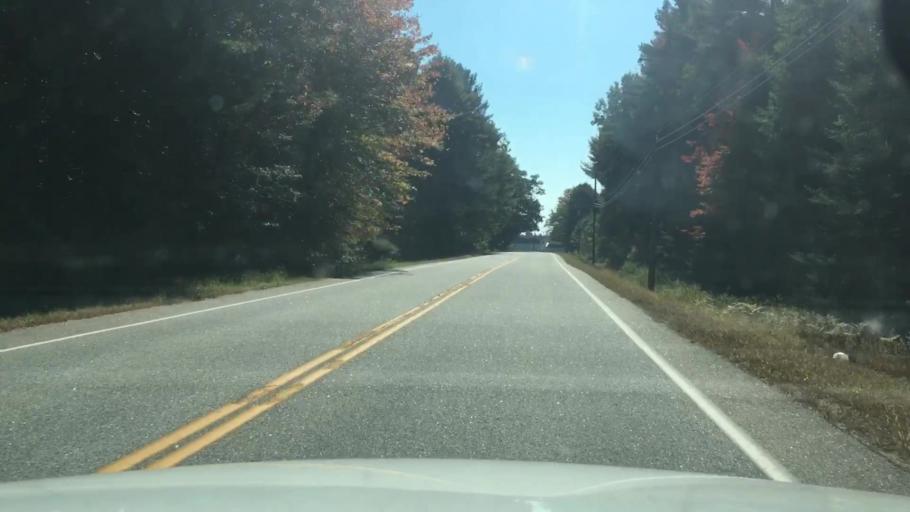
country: US
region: Maine
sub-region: Androscoggin County
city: Lisbon Falls
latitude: 44.0315
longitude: -70.0378
